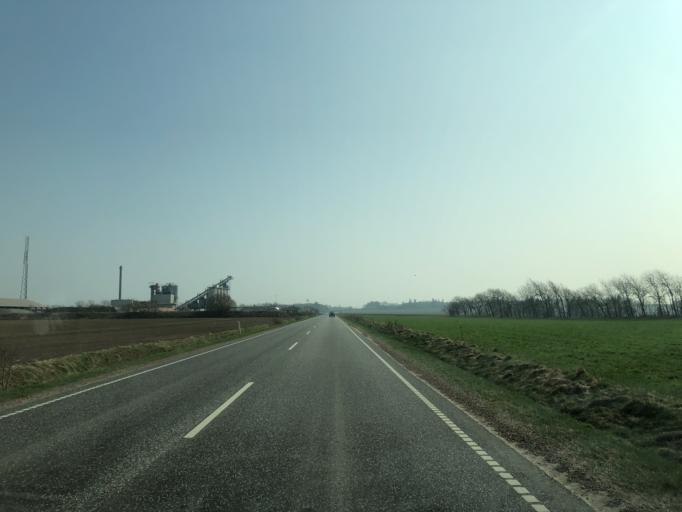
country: DK
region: Central Jutland
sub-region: Ringkobing-Skjern Kommune
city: Videbaek
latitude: 56.0943
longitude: 8.5076
